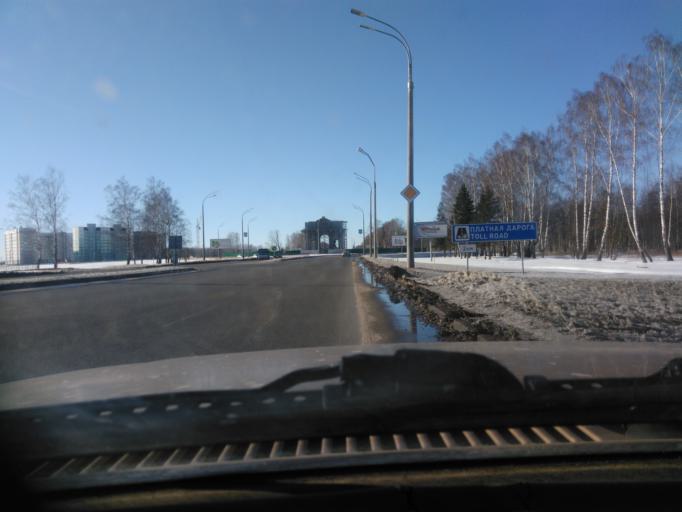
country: BY
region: Mogilev
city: Buynichy
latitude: 53.9353
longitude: 30.2531
